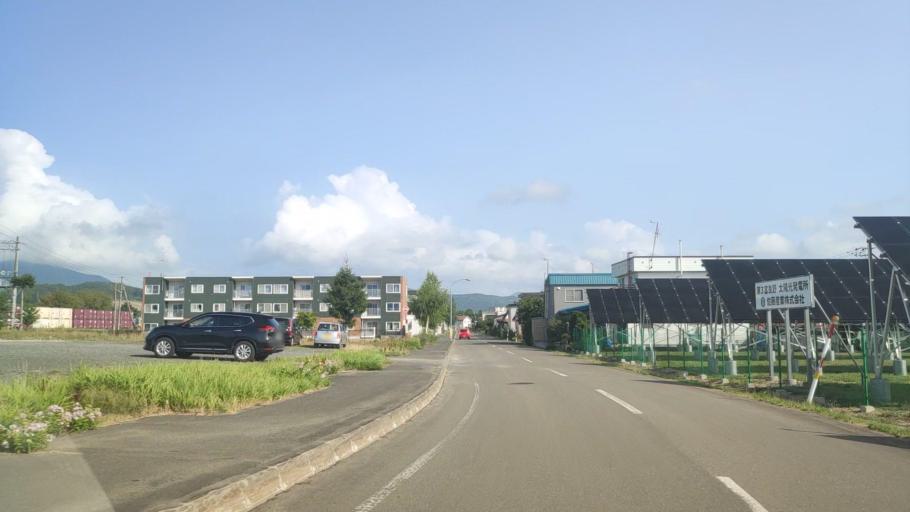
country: JP
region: Hokkaido
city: Shimo-furano
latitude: 43.3495
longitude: 142.3910
